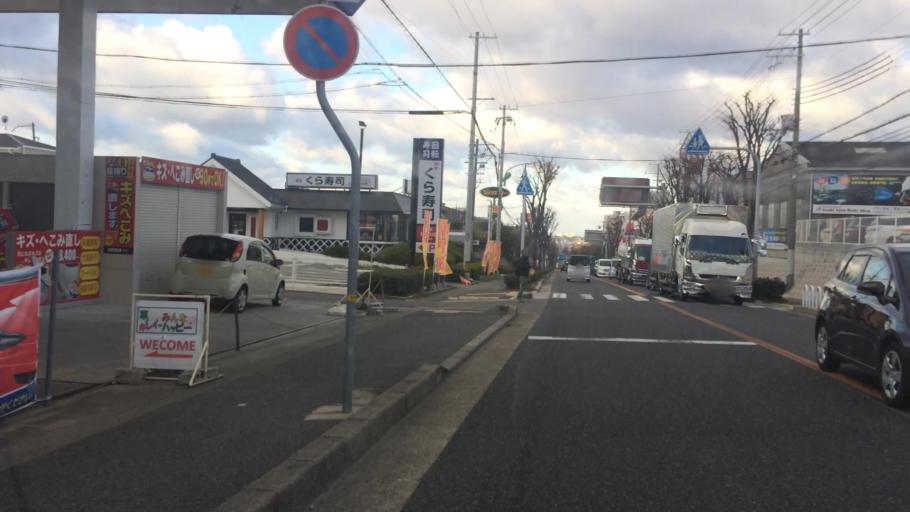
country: JP
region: Hyogo
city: Akashi
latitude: 34.6624
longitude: 135.0224
